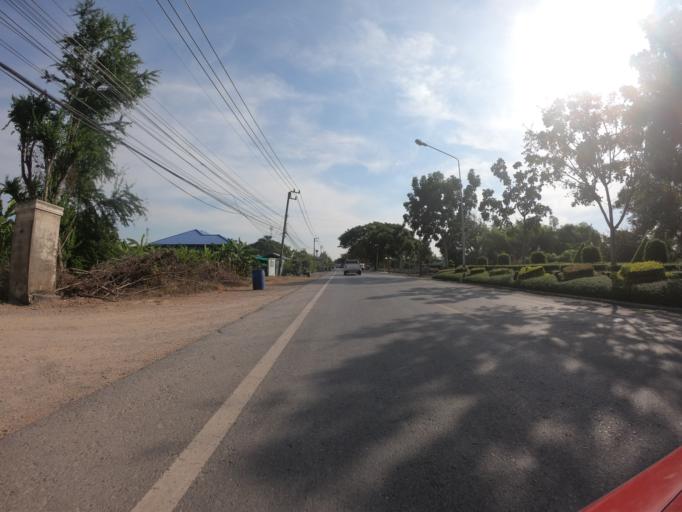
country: TH
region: Pathum Thani
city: Lam Luk Ka
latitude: 13.9706
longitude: 100.7283
